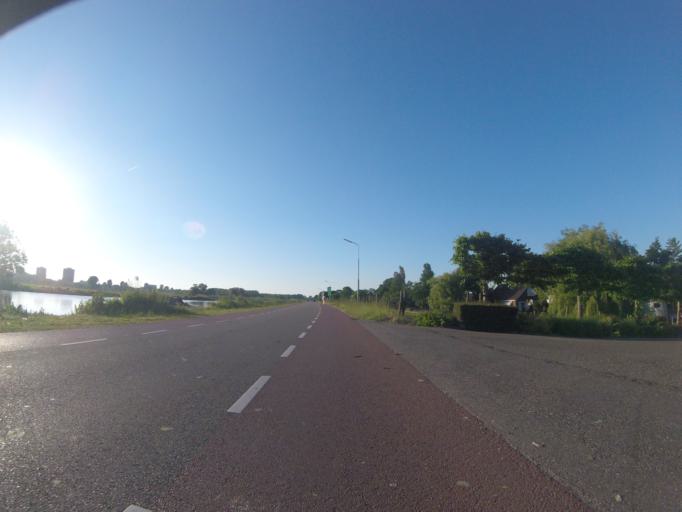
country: NL
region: North Holland
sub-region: Gemeente Haarlem
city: Haarlem
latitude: 52.3566
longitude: 4.6771
